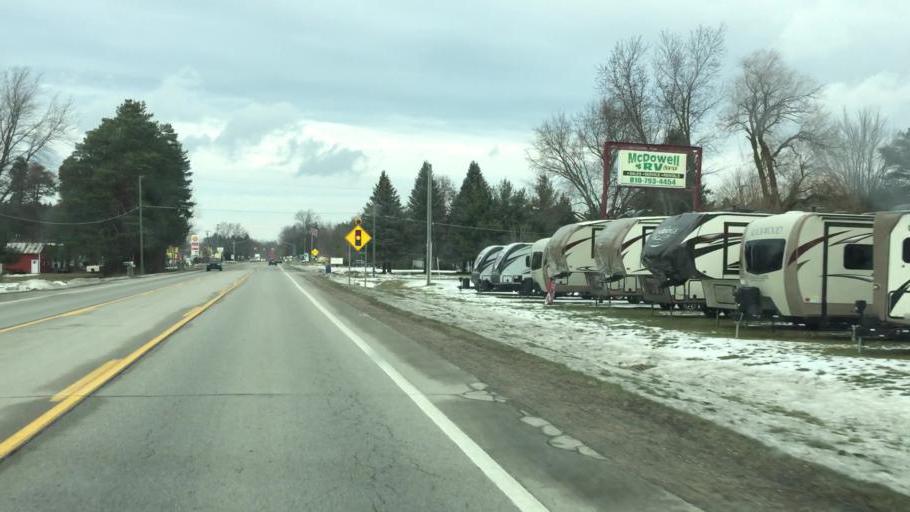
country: US
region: Michigan
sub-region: Lapeer County
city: Barnes Lake-Millers Lake
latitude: 43.2005
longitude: -83.3128
